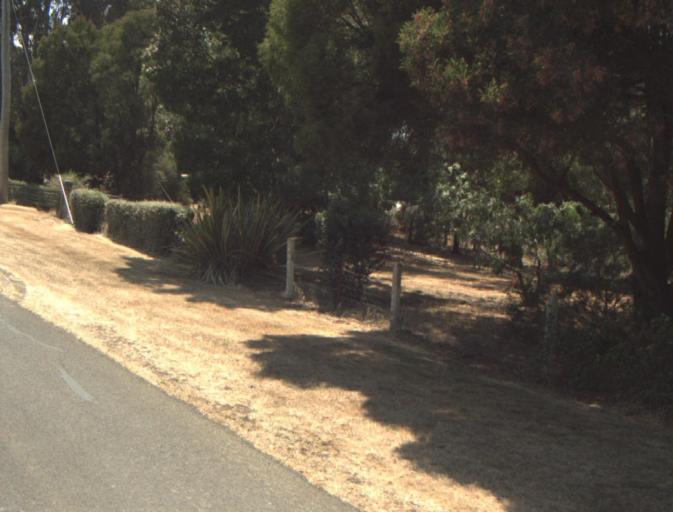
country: AU
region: Tasmania
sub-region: Launceston
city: Newstead
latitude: -41.4893
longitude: 147.1841
